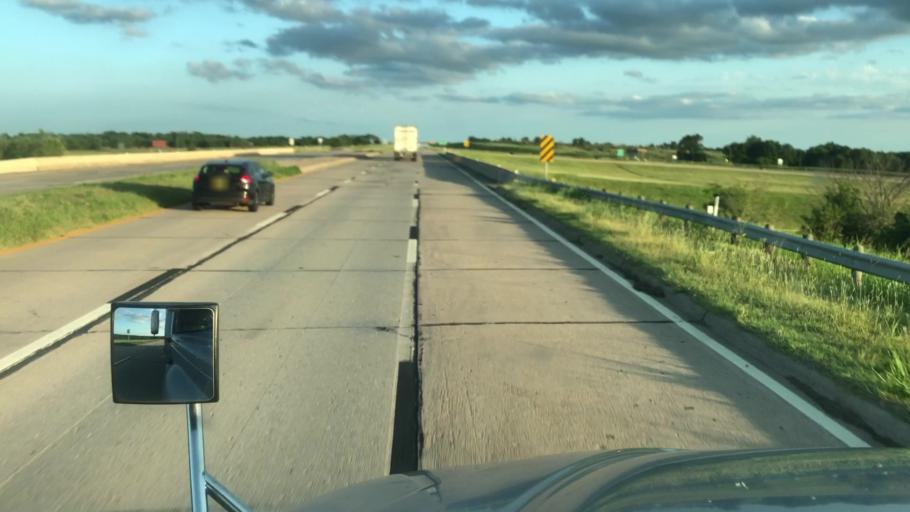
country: US
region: Oklahoma
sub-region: Pawnee County
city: Pawnee
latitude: 36.2987
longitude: -96.9873
